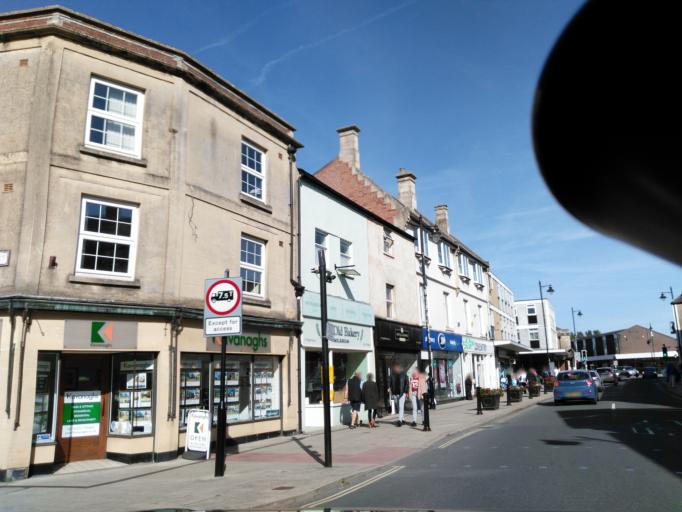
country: GB
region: England
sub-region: Wiltshire
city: Melksham
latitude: 51.3727
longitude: -2.1383
